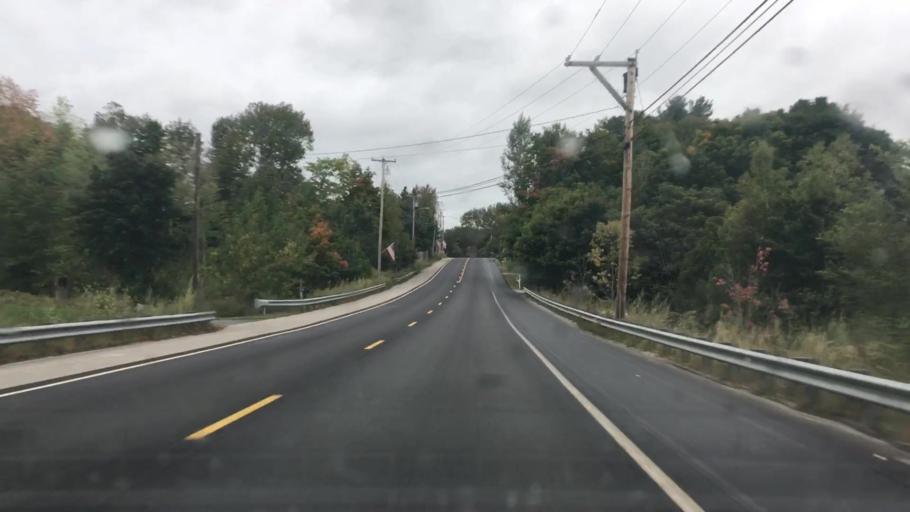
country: US
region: Maine
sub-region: Penobscot County
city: Orrington
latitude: 44.7529
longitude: -68.8001
